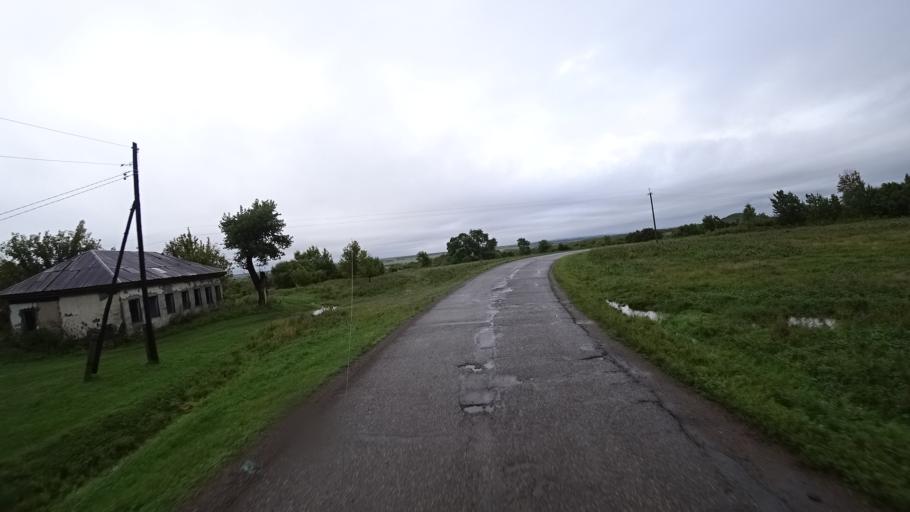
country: RU
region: Primorskiy
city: Monastyrishche
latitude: 44.2706
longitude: 132.4206
